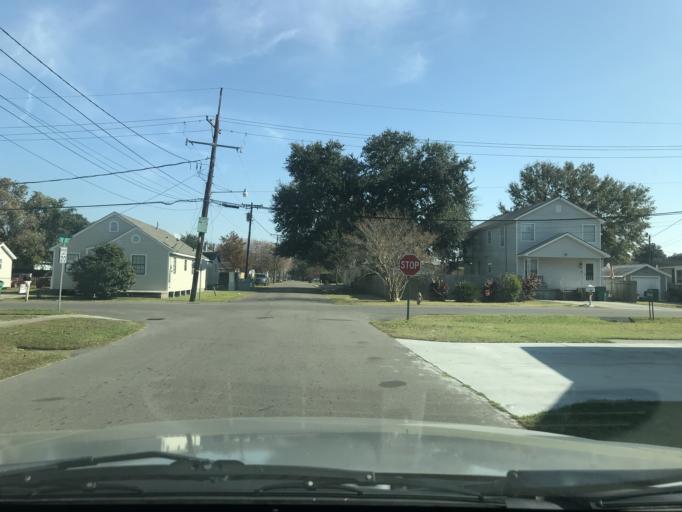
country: US
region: Louisiana
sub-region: Jefferson Parish
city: Marrero
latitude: 29.8939
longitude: -90.0931
